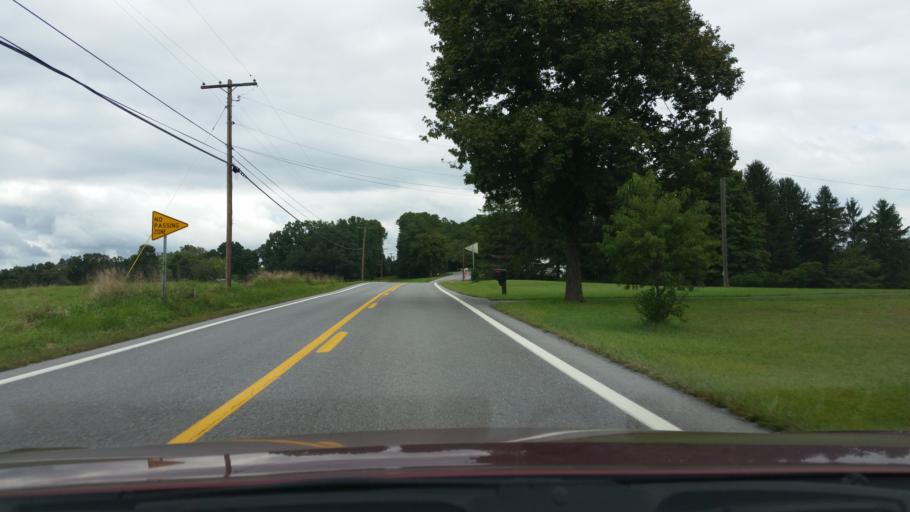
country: US
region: Maryland
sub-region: Washington County
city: Hancock
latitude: 39.6369
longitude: -78.1590
